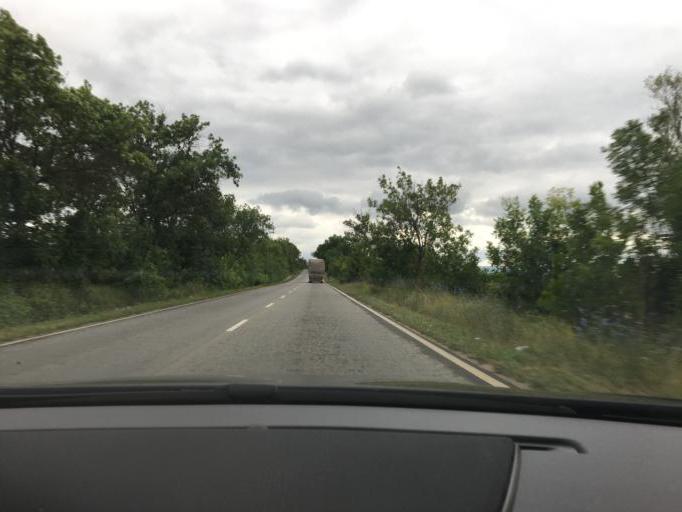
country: BG
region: Kyustendil
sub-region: Obshtina Kyustendil
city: Kyustendil
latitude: 42.2709
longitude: 22.7808
